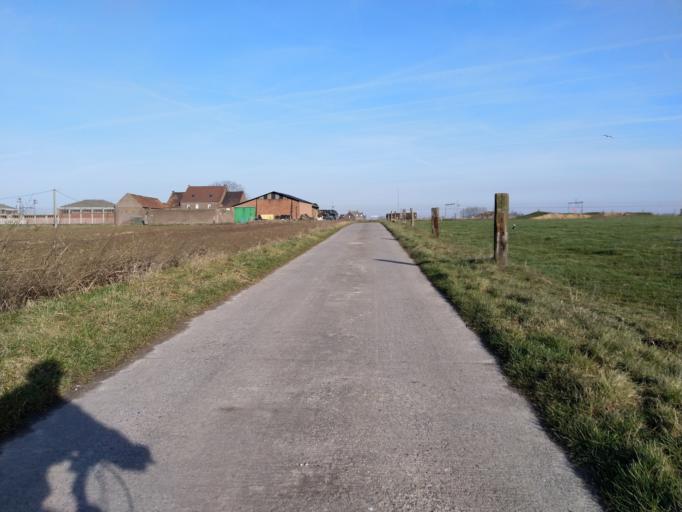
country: BE
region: Wallonia
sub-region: Province du Hainaut
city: Jurbise
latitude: 50.5338
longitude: 3.9262
